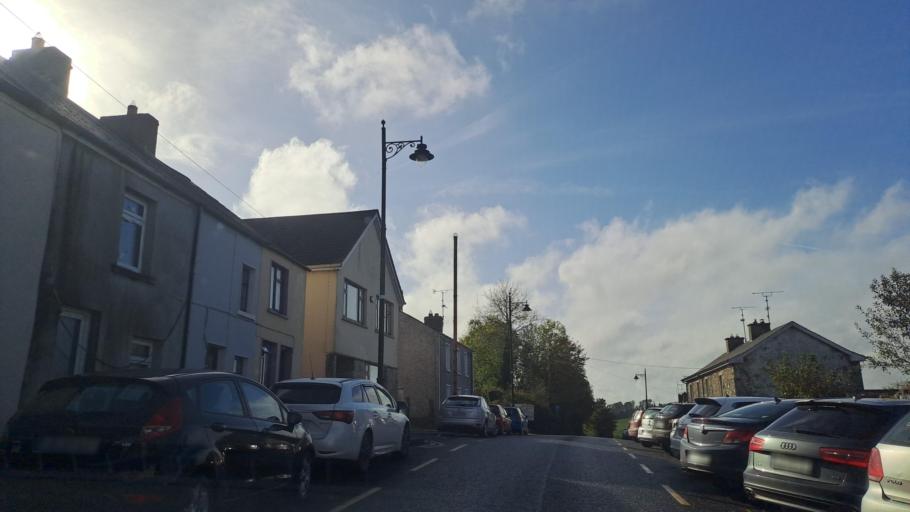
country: IE
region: Ulster
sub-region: An Cabhan
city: Cootehill
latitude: 54.0722
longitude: -7.0828
